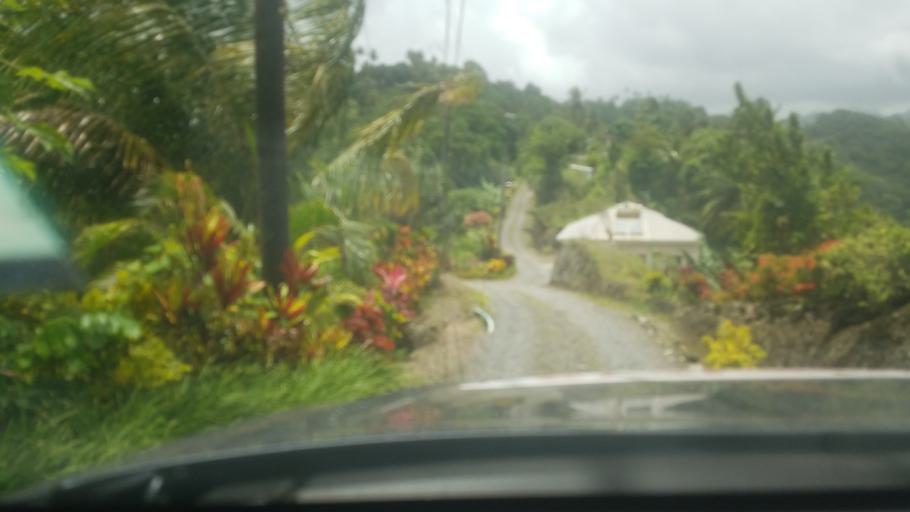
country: LC
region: Laborie Quarter
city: Laborie
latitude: 13.7814
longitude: -60.9926
